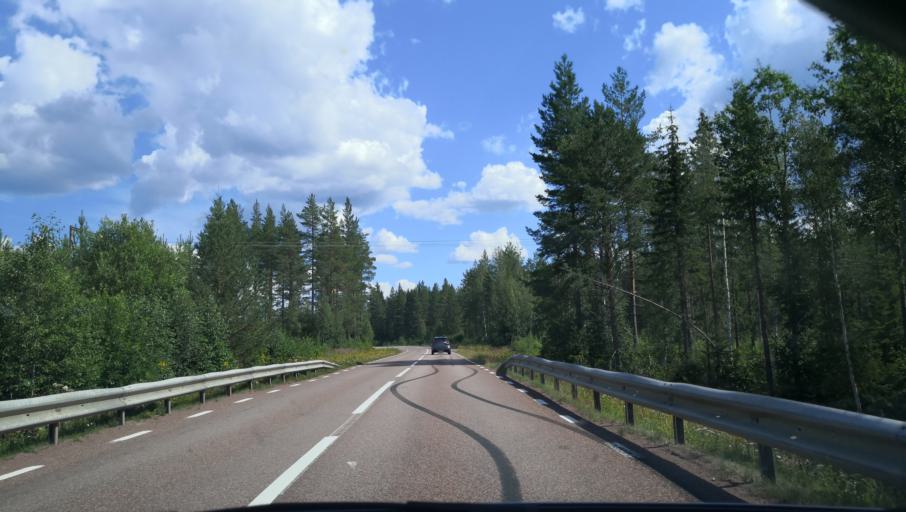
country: SE
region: Dalarna
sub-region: Rattviks Kommun
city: Vikarbyn
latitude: 61.1435
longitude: 15.1213
